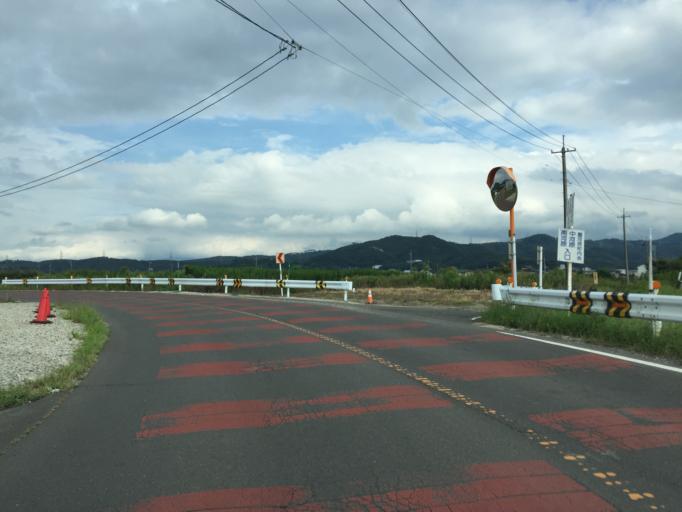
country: JP
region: Fukushima
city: Fukushima-shi
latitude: 37.7873
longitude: 140.4970
